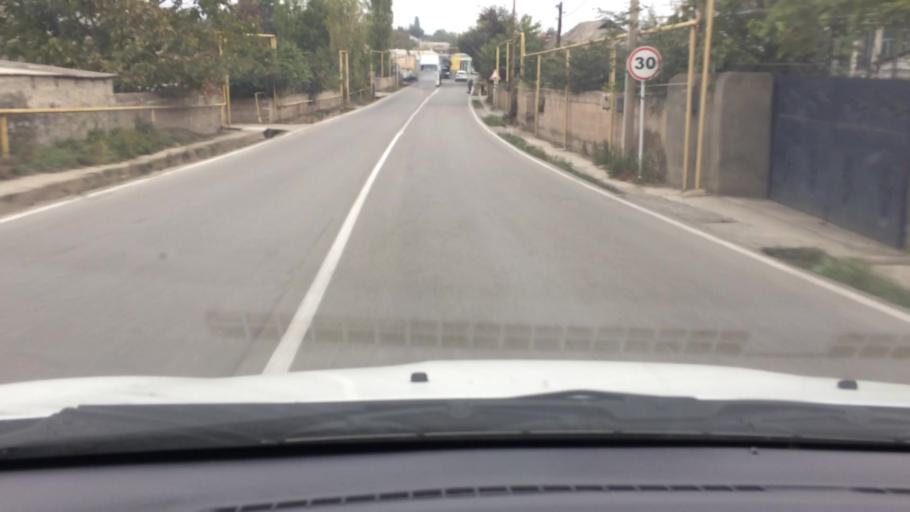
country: AM
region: Tavush
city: Bagratashen
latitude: 41.2436
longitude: 44.7981
